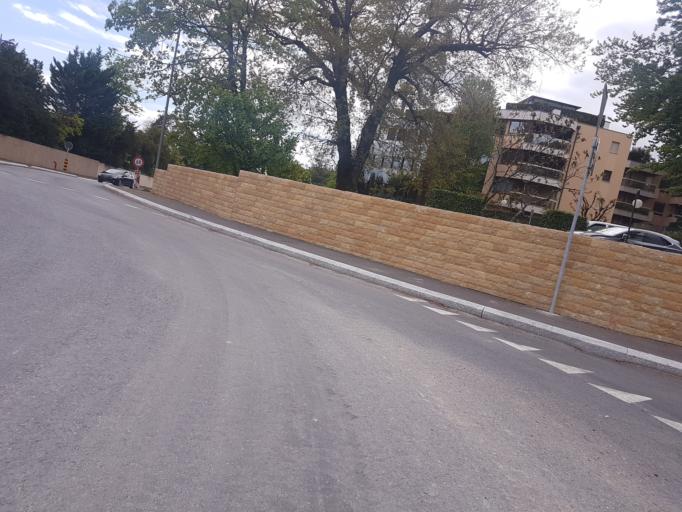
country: CH
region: Vaud
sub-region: Nyon District
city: Coppet
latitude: 46.3085
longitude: 6.1834
